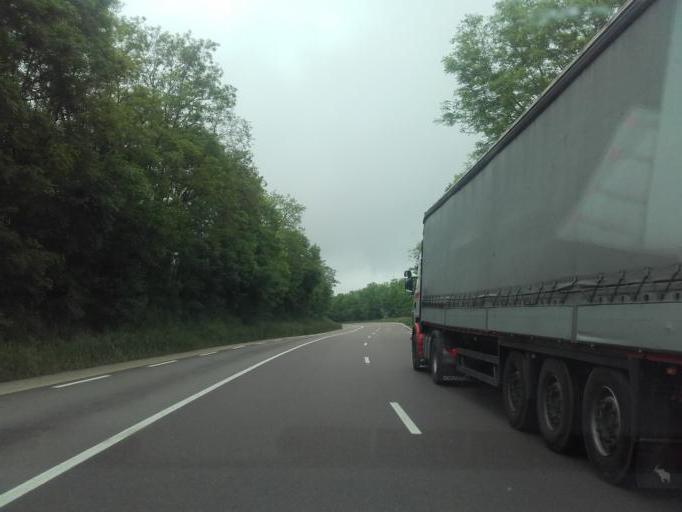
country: FR
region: Bourgogne
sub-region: Departement de la Cote-d'Or
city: Nolay
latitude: 46.9620
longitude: 4.6744
